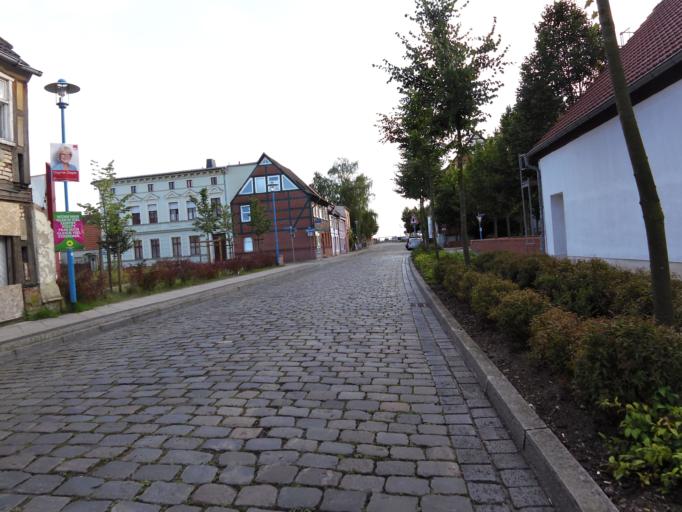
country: DE
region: Brandenburg
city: Wittenberge
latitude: 52.9917
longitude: 11.7522
